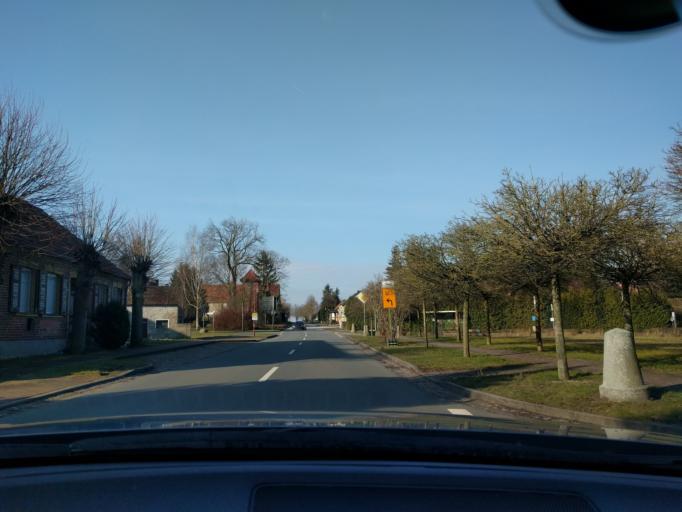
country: DE
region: Saxony-Anhalt
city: Iden
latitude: 52.7536
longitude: 11.9328
